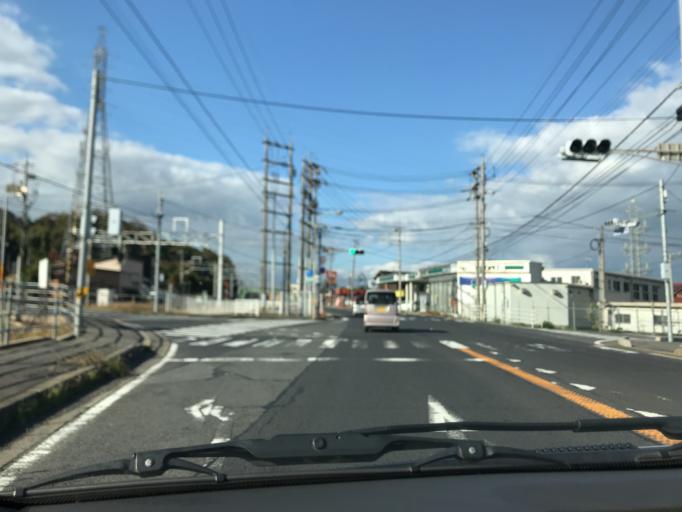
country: JP
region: Shimane
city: Yasugicho
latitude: 35.4285
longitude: 133.2652
